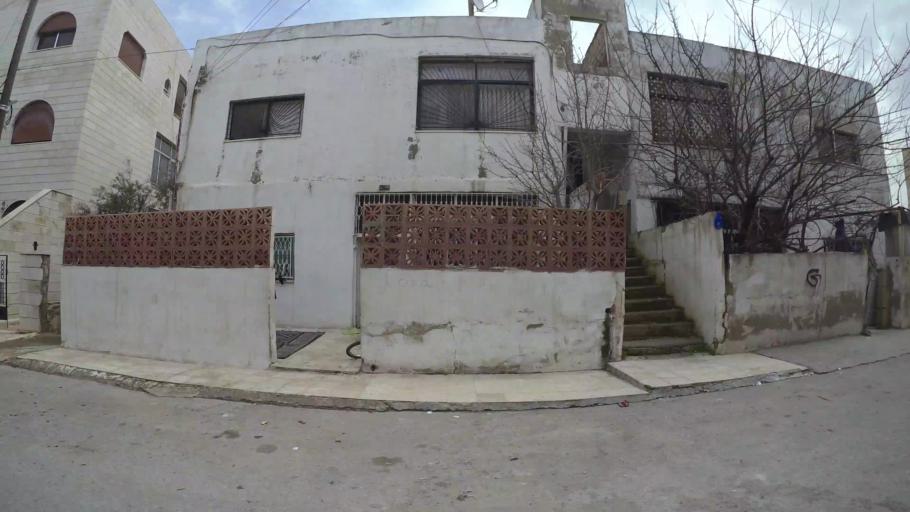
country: JO
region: Amman
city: Umm as Summaq
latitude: 31.8965
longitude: 35.8391
